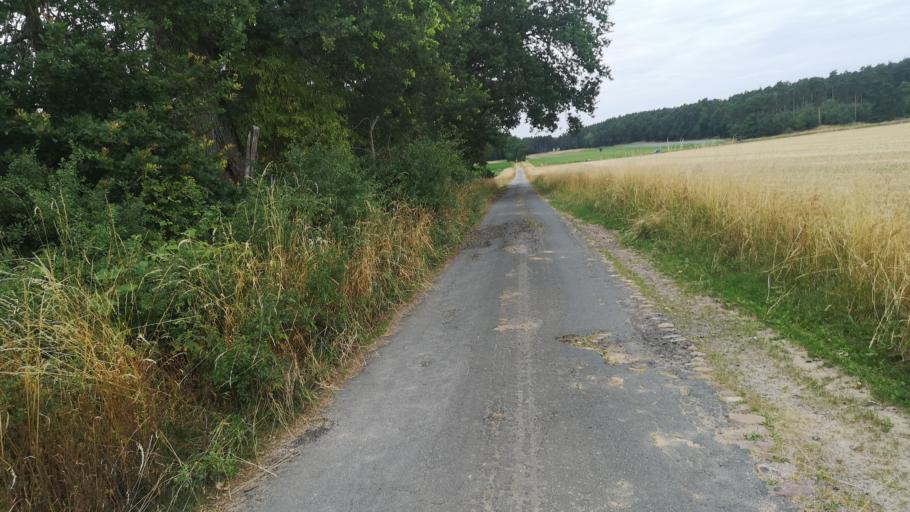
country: DE
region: Lower Saxony
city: Dahlem
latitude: 53.2157
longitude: 10.7495
